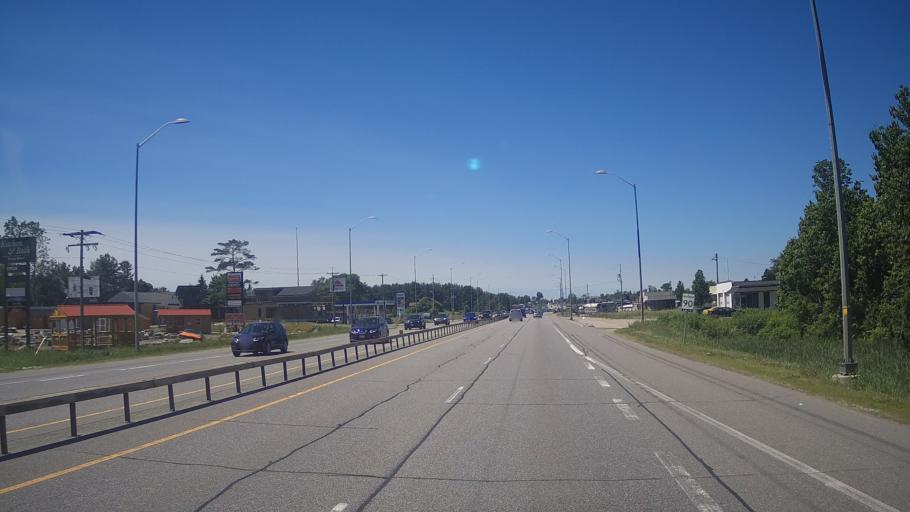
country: CA
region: Ontario
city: Barrie
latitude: 44.4456
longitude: -79.6117
